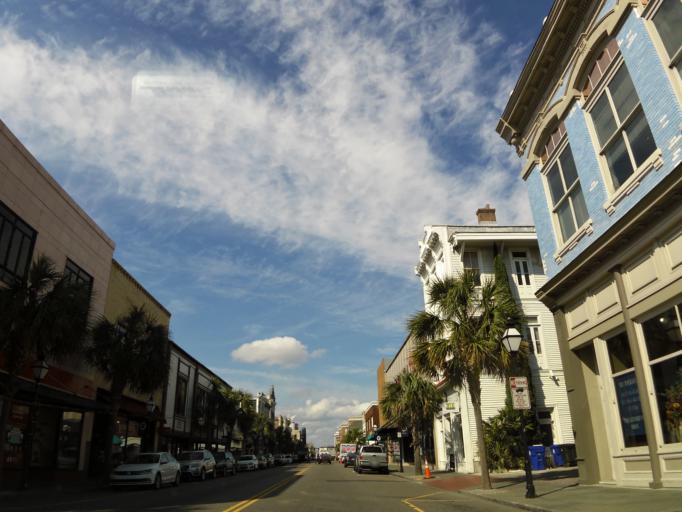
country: US
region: South Carolina
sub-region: Charleston County
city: Charleston
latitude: 32.7905
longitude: -79.9395
